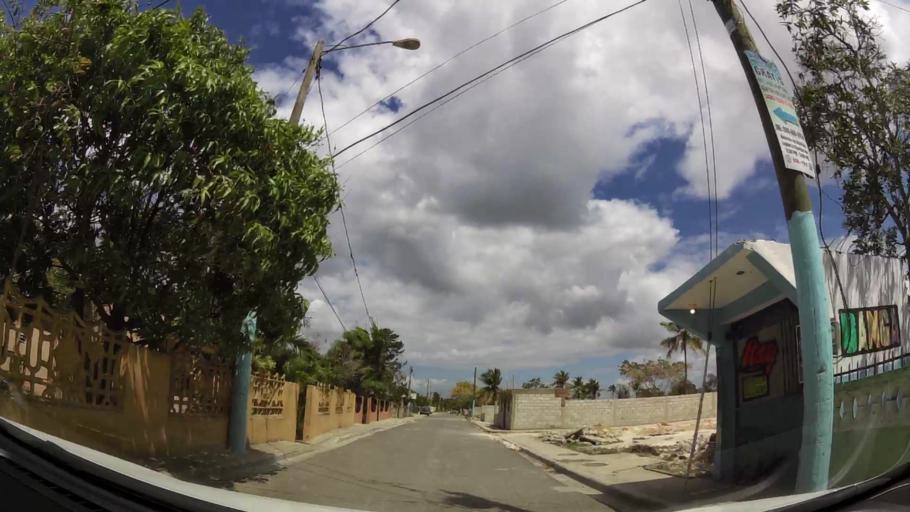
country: DO
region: Santo Domingo
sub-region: Santo Domingo
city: Boca Chica
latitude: 18.4511
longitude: -69.6559
